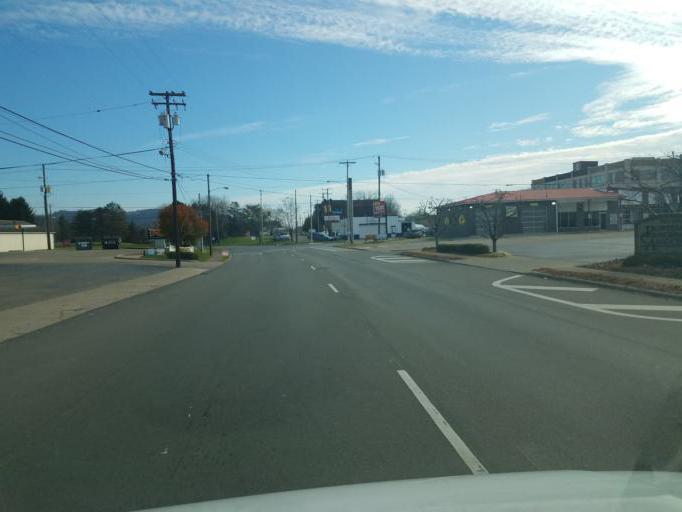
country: US
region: Ohio
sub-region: Scioto County
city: Portsmouth
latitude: 38.7392
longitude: -82.9938
